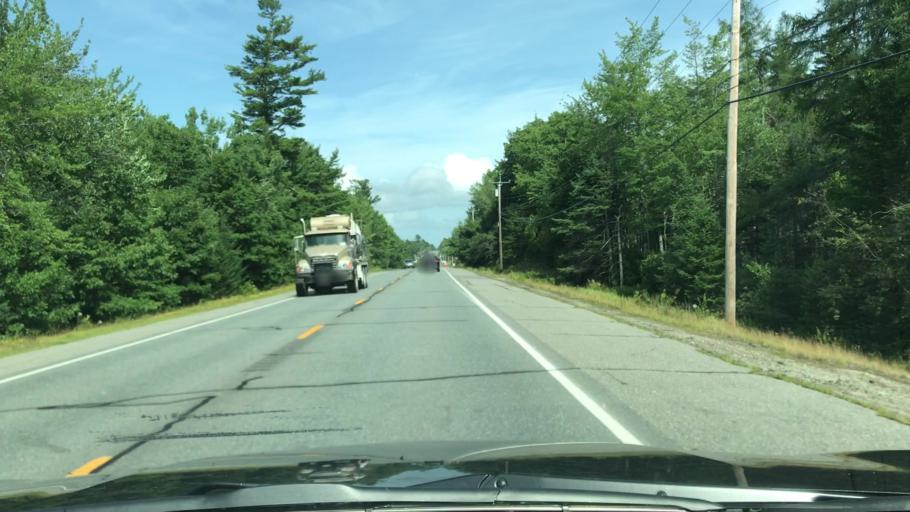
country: US
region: Maine
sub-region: Hancock County
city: Ellsworth
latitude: 44.5395
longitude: -68.4654
